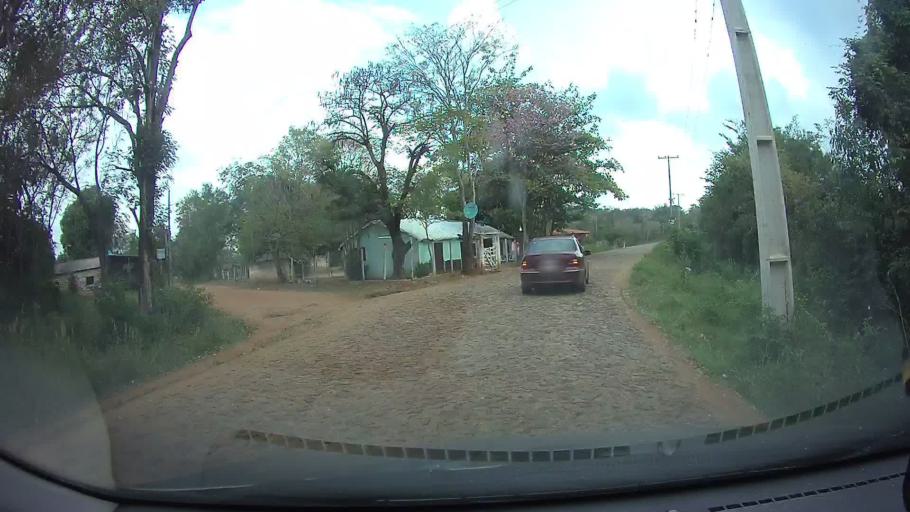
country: PY
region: Cordillera
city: Arroyos y Esteros
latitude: -25.0214
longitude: -57.1159
